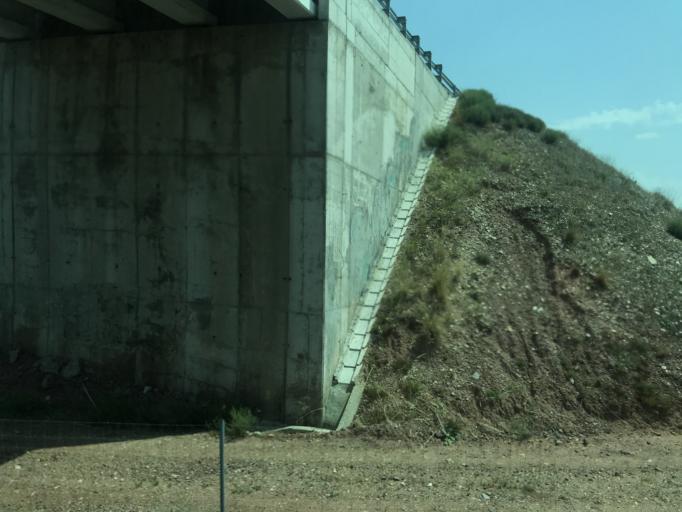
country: ES
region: Castille and Leon
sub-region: Provincia de Segovia
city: Honrubia de la Cuesta
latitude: 41.4826
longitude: -3.6947
